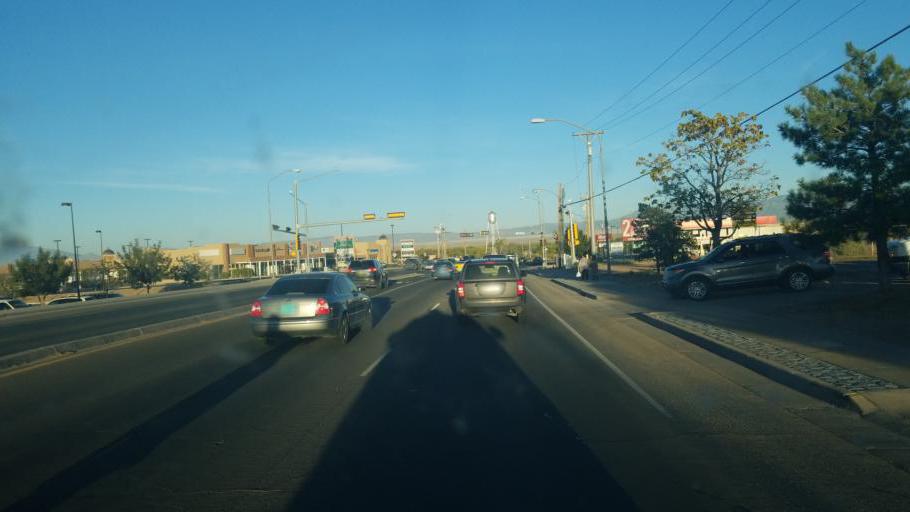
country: US
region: New Mexico
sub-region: Valencia County
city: Los Lunas
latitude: 34.8144
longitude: -106.7514
